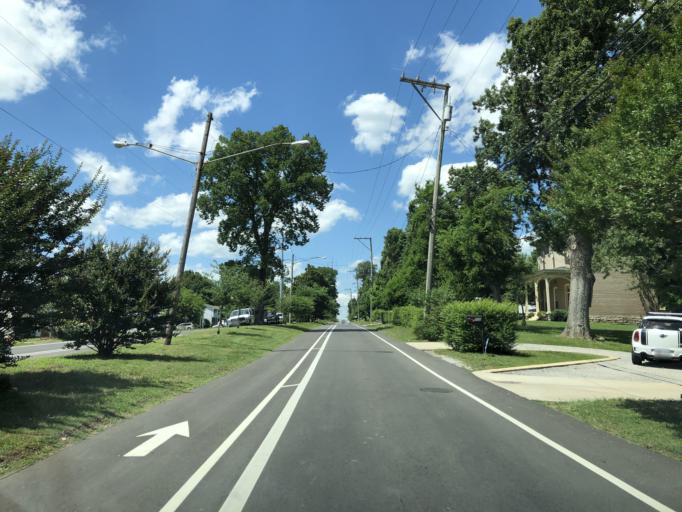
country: US
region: Tennessee
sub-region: Davidson County
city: Nashville
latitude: 36.1782
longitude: -86.7260
